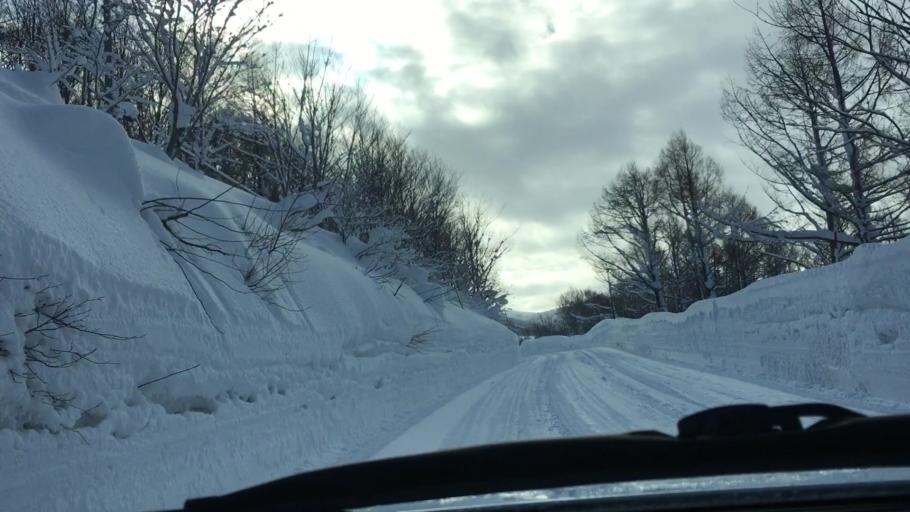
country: JP
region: Aomori
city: Aomori Shi
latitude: 40.6478
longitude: 140.7824
